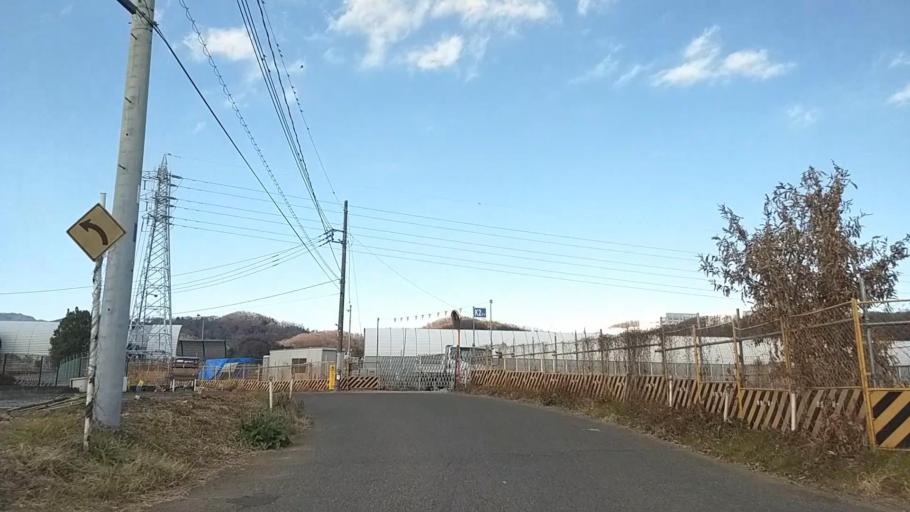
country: JP
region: Kanagawa
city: Isehara
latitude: 35.4122
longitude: 139.3174
